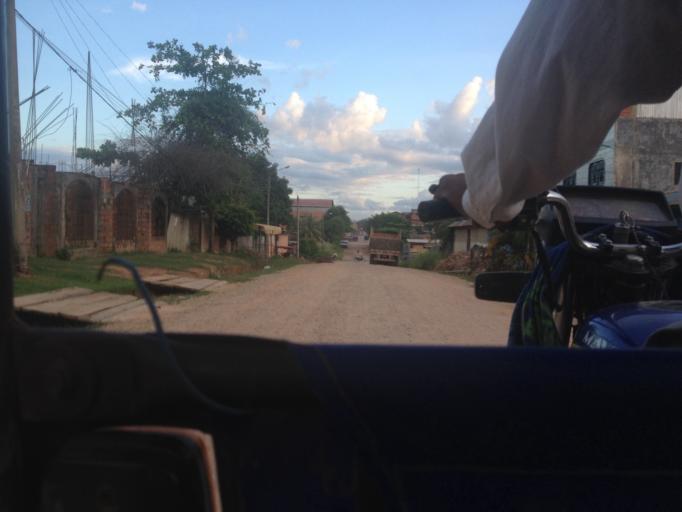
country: PE
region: Ucayali
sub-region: Provincia de Coronel Portillo
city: Pucallpa
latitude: -8.3820
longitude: -74.5688
